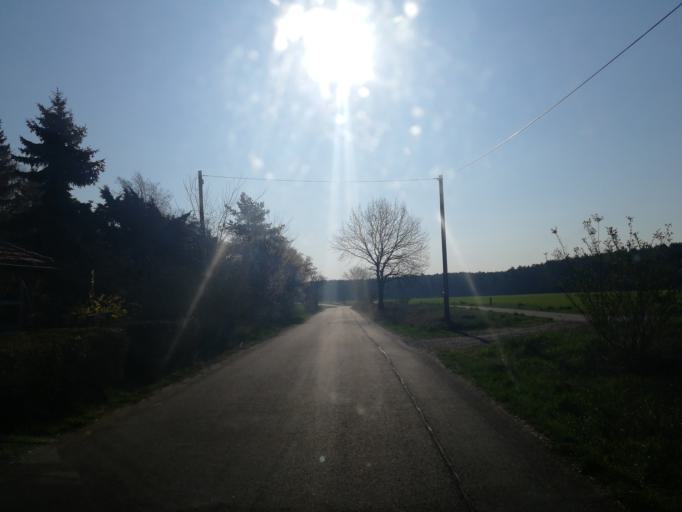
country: DE
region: Brandenburg
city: Drahnsdorf
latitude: 51.8954
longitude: 13.5625
